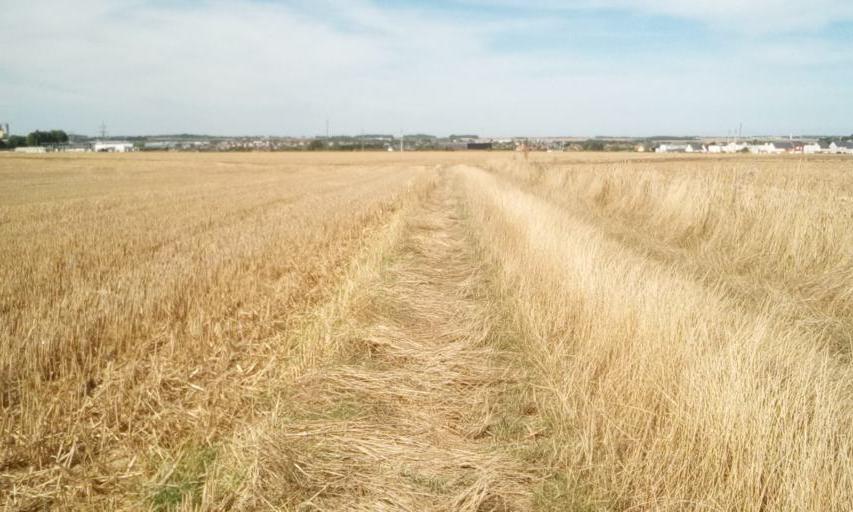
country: FR
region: Lower Normandy
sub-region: Departement du Calvados
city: Fontaine-Etoupefour
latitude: 49.1348
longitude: -0.4552
